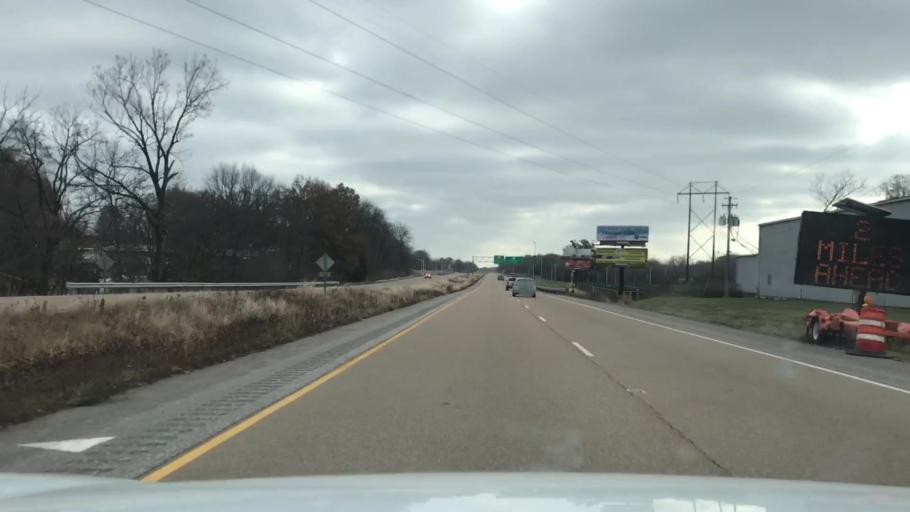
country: US
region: Illinois
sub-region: Saint Clair County
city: Belleville
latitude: 38.5080
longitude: -90.0070
